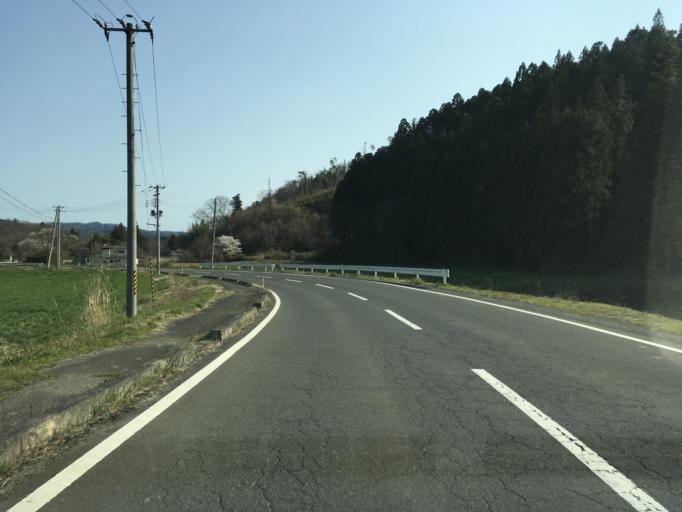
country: JP
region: Iwate
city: Ichinoseki
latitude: 38.7972
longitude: 141.3190
